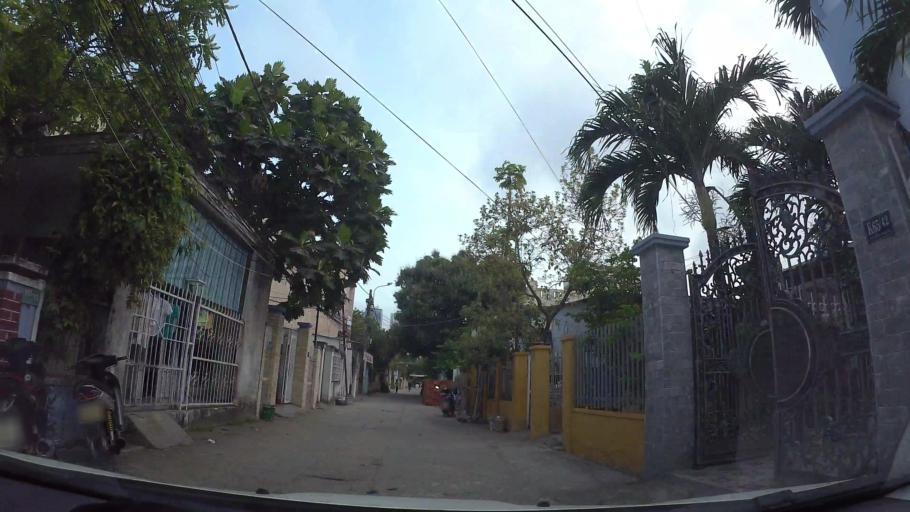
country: VN
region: Da Nang
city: Son Tra
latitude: 16.0605
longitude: 108.2442
